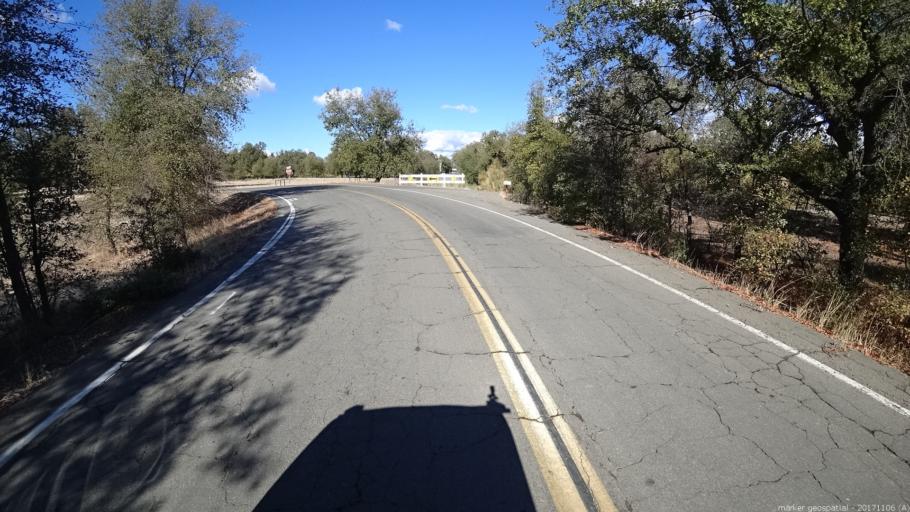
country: US
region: California
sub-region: Shasta County
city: Palo Cedro
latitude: 40.5954
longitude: -122.2345
